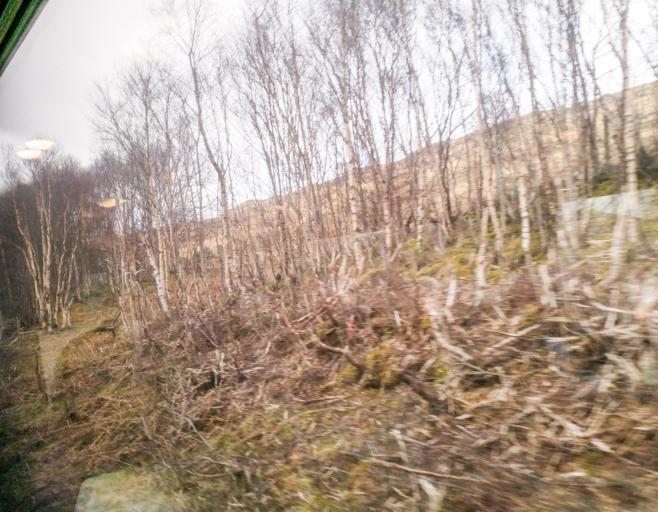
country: GB
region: Scotland
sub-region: Highland
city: Spean Bridge
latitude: 56.7827
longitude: -4.7327
